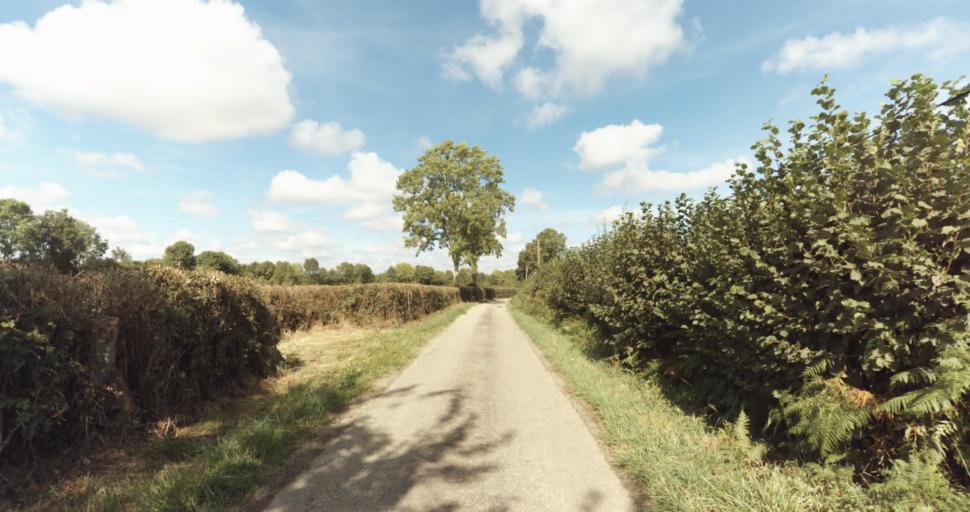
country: FR
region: Lower Normandy
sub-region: Departement du Calvados
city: Orbec
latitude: 48.9682
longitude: 0.3803
